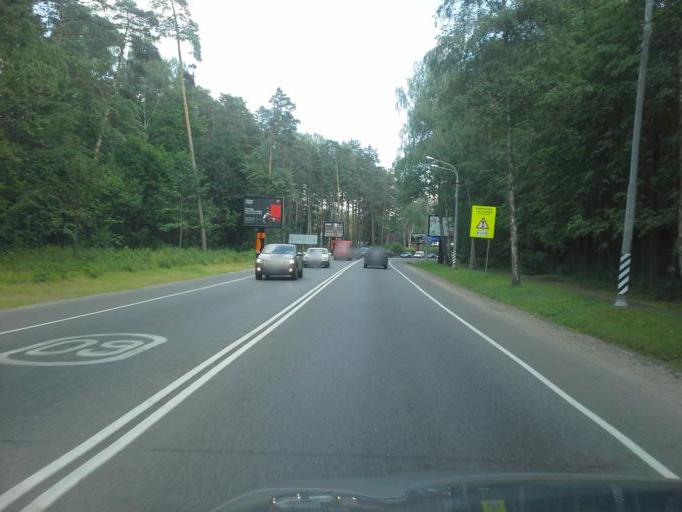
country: RU
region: Moskovskaya
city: Barvikha
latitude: 55.7376
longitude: 37.2382
